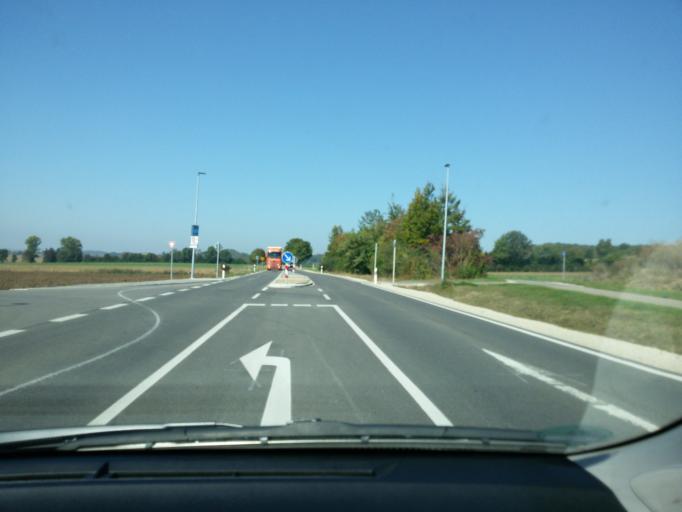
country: DE
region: Bavaria
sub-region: Swabia
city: Oettingen in Bayern
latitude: 48.9588
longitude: 10.5908
